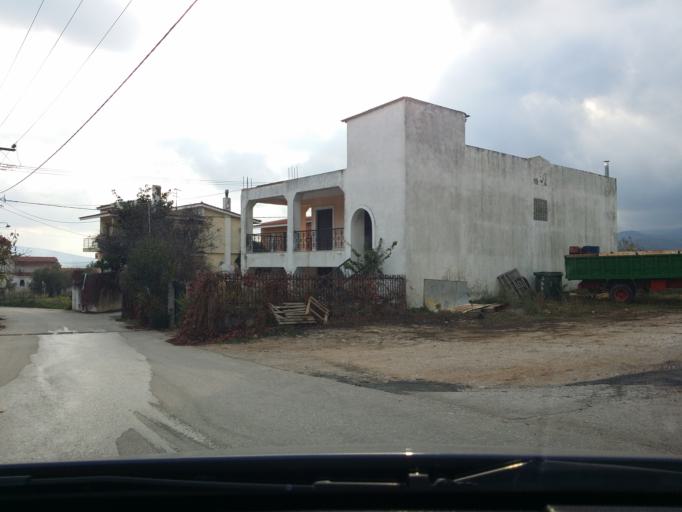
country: GR
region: Attica
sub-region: Nomarchia Anatolikis Attikis
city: Polydendri
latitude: 38.2167
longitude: 23.8660
